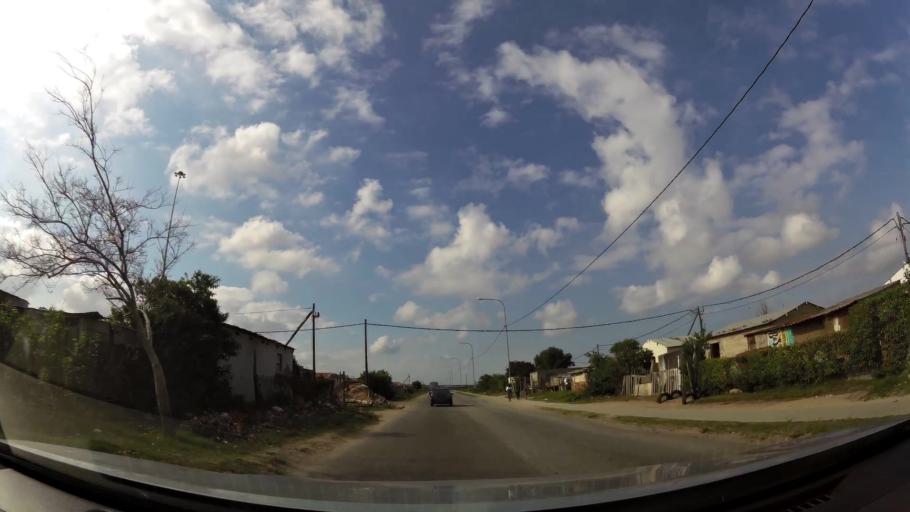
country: ZA
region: Eastern Cape
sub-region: Nelson Mandela Bay Metropolitan Municipality
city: Port Elizabeth
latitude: -33.7869
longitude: 25.5885
